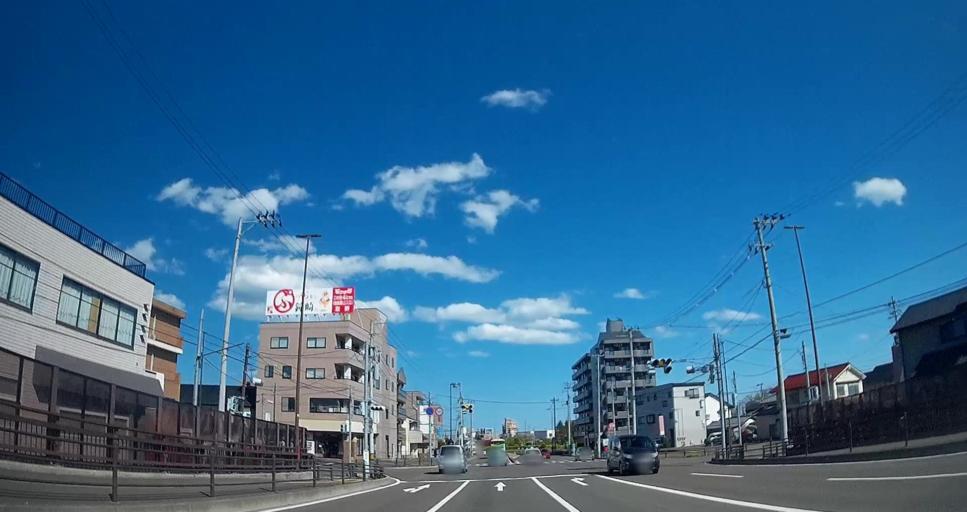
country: JP
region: Miyagi
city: Sendai-shi
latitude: 38.2527
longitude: 140.9078
